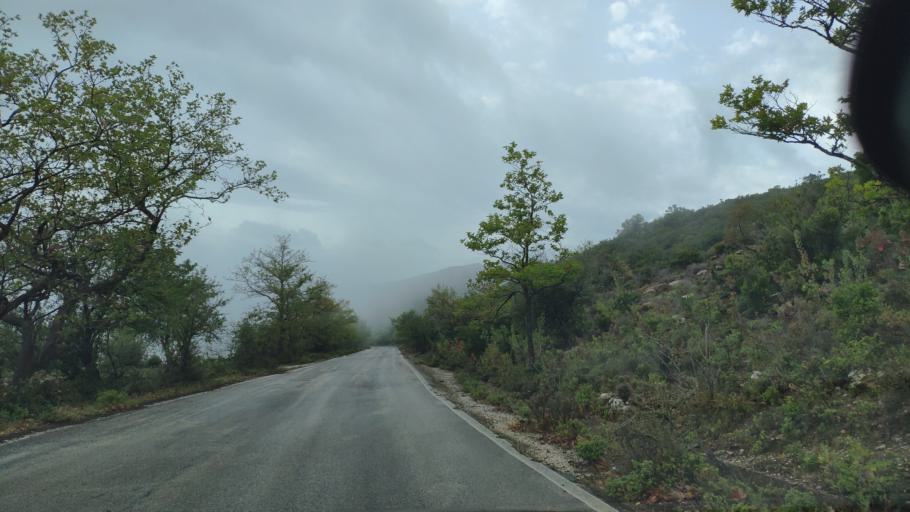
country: GR
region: West Greece
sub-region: Nomos Aitolias kai Akarnanias
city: Sardinia
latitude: 38.8508
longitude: 21.3152
